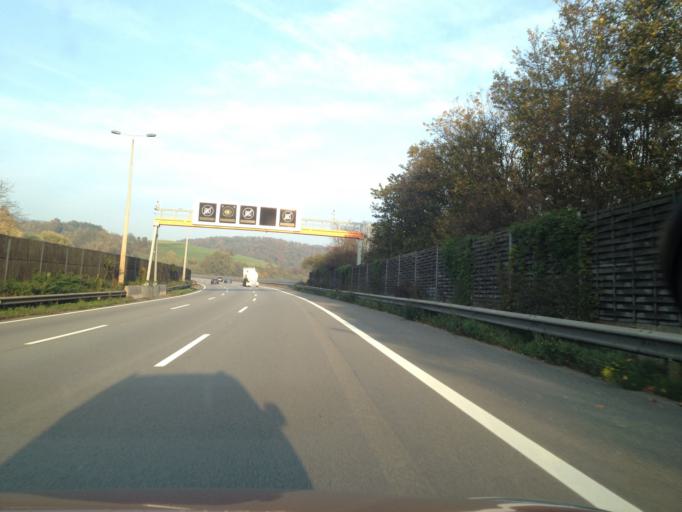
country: AT
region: Upper Austria
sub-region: Linz Stadt
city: Linz
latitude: 48.3267
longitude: 14.3194
